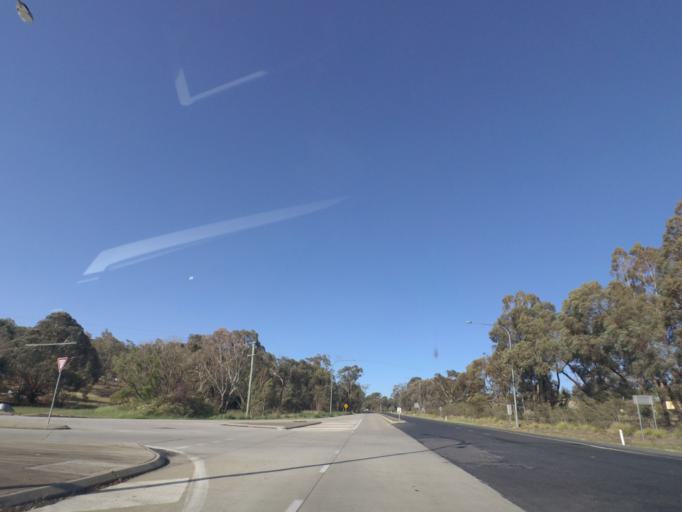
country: AU
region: New South Wales
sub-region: Wagga Wagga
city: Forest Hill
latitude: -35.2756
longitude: 147.7390
